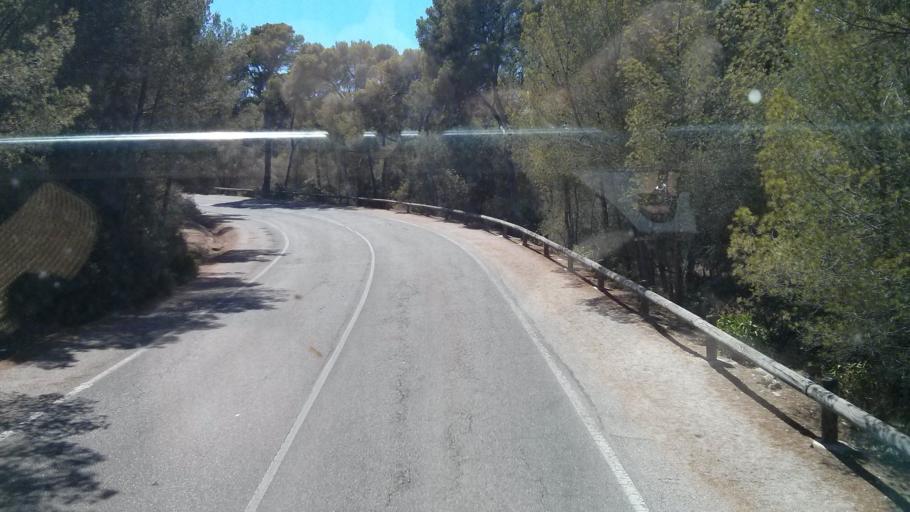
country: ES
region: Balearic Islands
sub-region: Illes Balears
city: Palma
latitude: 39.5666
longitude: 2.6155
